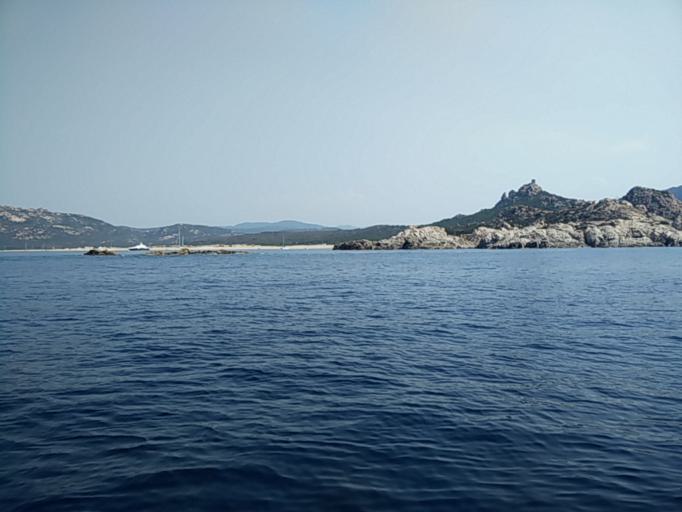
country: FR
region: Corsica
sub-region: Departement de la Corse-du-Sud
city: Sartene
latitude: 41.4874
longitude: 8.9179
